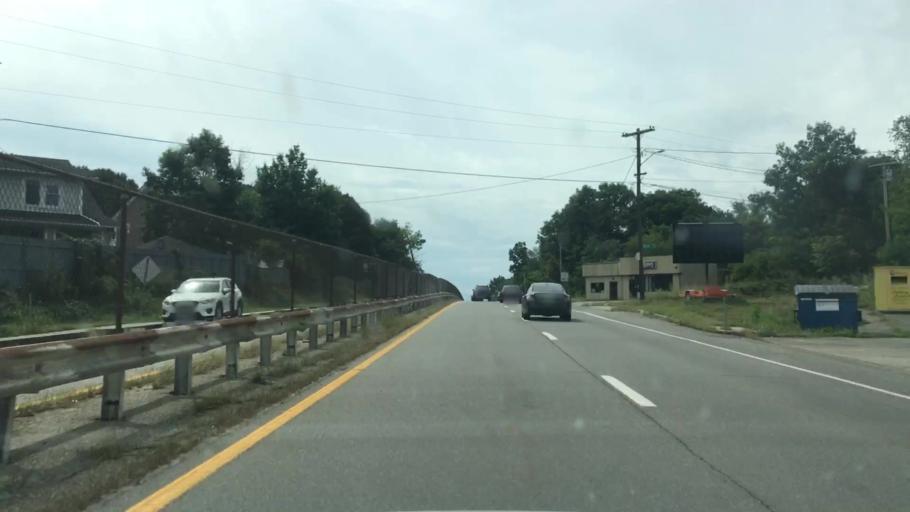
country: US
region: New Hampshire
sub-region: Rockingham County
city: Portsmouth
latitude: 43.0788
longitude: -70.7725
